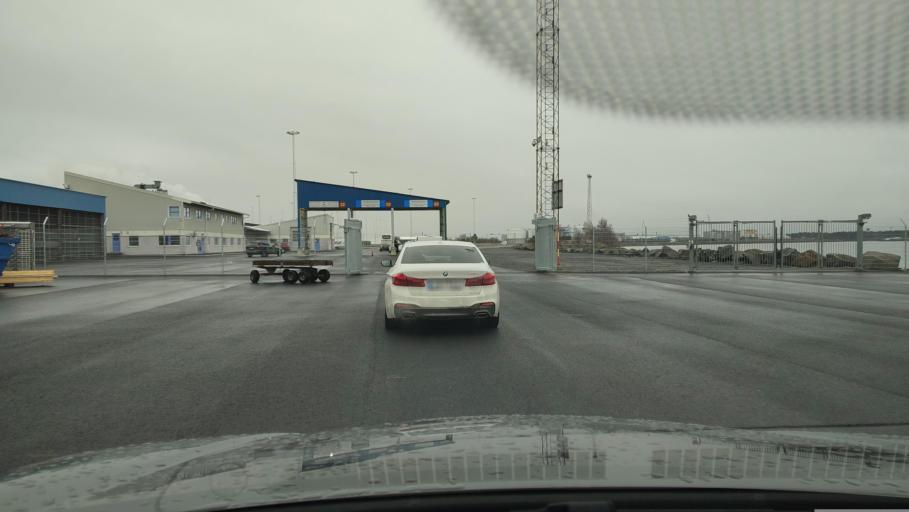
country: SE
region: Vaesterbotten
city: Obbola
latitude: 63.6824
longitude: 20.3406
